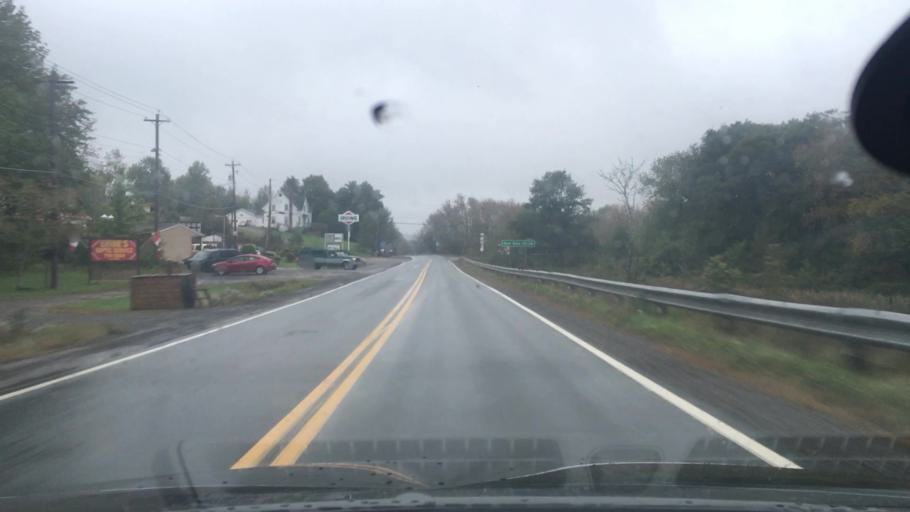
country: CA
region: Nova Scotia
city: Windsor
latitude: 44.8420
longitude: -64.2302
